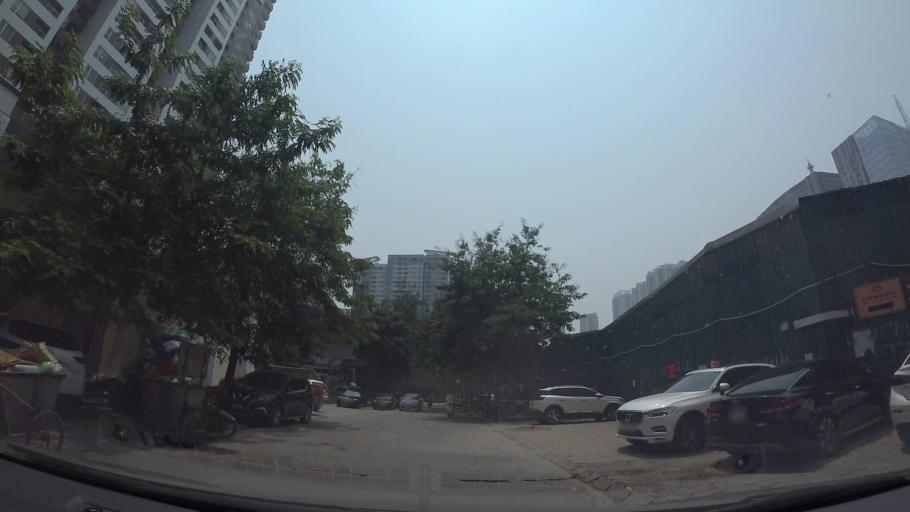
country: VN
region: Ha Noi
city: Thanh Xuan
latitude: 21.0078
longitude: 105.8008
